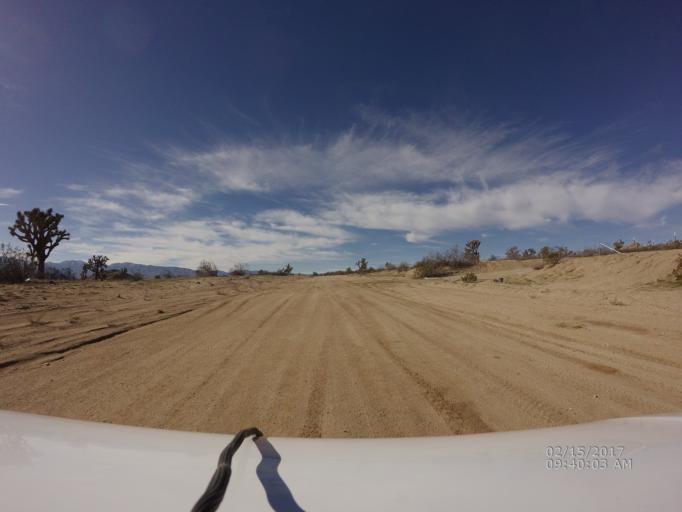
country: US
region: California
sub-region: Los Angeles County
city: Lake Los Angeles
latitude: 34.6273
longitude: -117.8873
